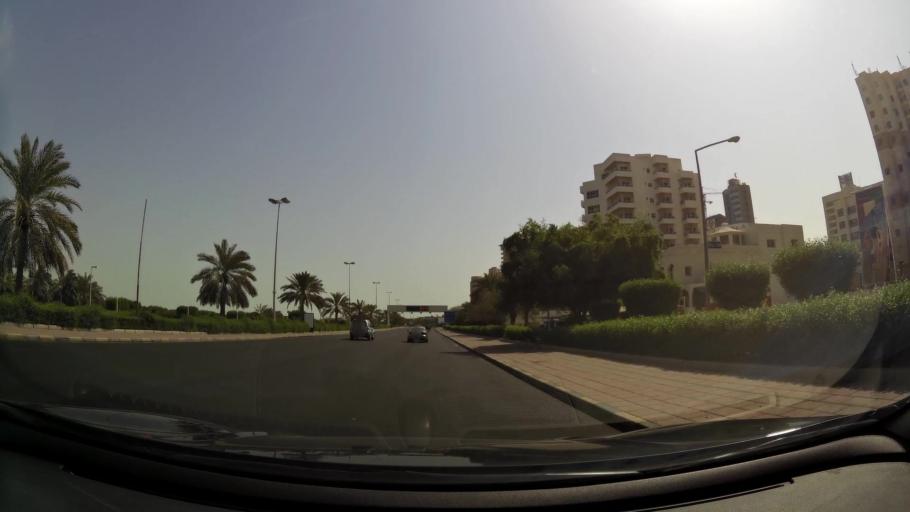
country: KW
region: Al Asimah
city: Ad Dasmah
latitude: 29.3715
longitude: 48.0087
